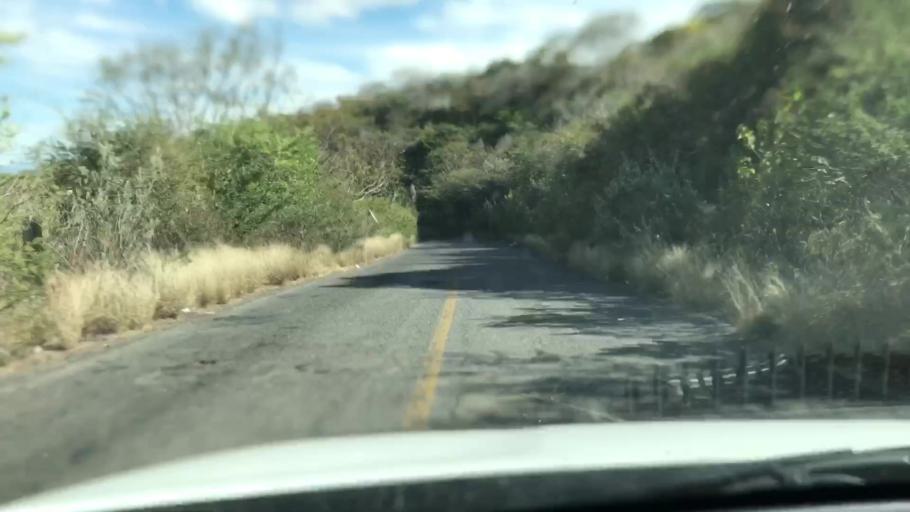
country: MX
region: Jalisco
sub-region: Zacoalco de Torres
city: Barranca de Otates (Barranca de Otatan)
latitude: 20.2572
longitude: -103.6752
